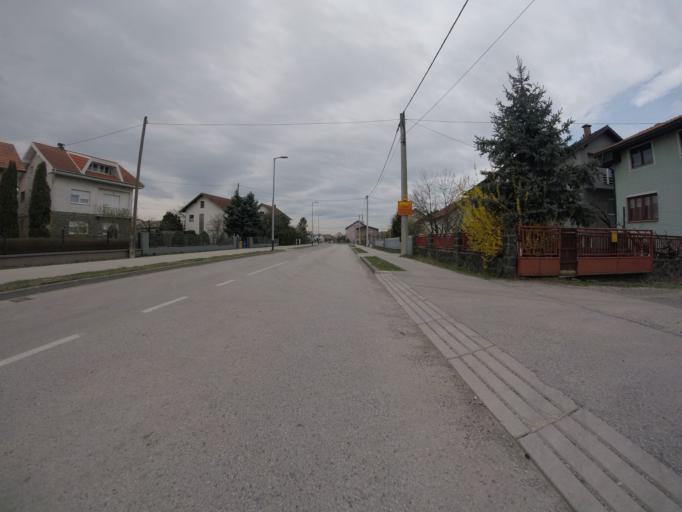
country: HR
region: Zagrebacka
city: Gradici
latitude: 45.7078
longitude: 16.0426
